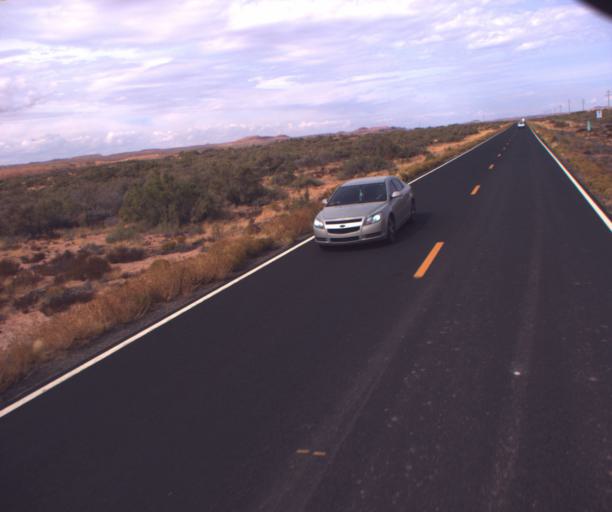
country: US
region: Arizona
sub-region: Apache County
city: Many Farms
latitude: 36.6347
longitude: -109.5865
